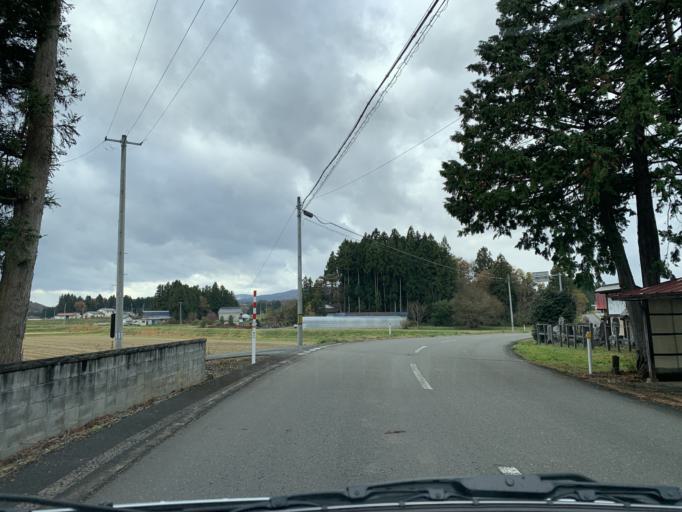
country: JP
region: Iwate
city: Mizusawa
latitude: 39.0728
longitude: 141.0626
